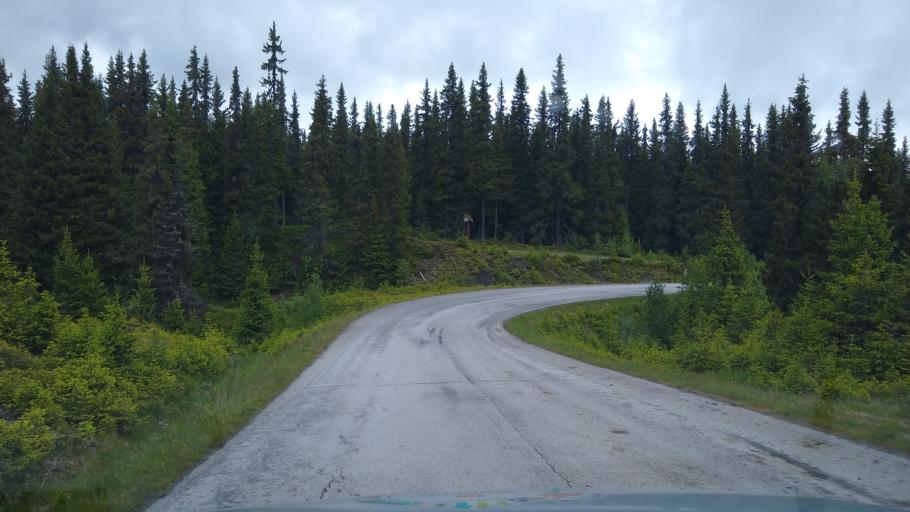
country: NO
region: Oppland
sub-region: Ringebu
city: Ringebu
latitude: 61.4910
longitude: 10.1136
